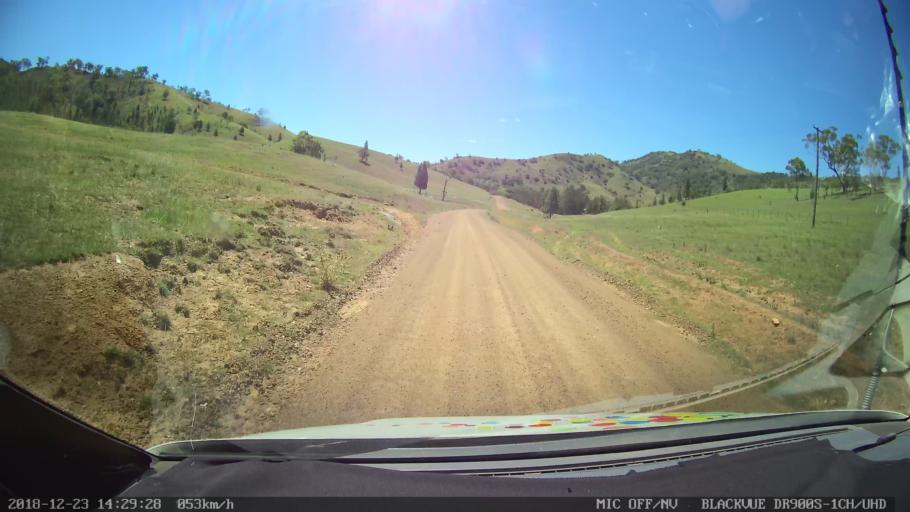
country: AU
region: New South Wales
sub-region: Tamworth Municipality
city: Manilla
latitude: -30.6083
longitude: 150.9376
